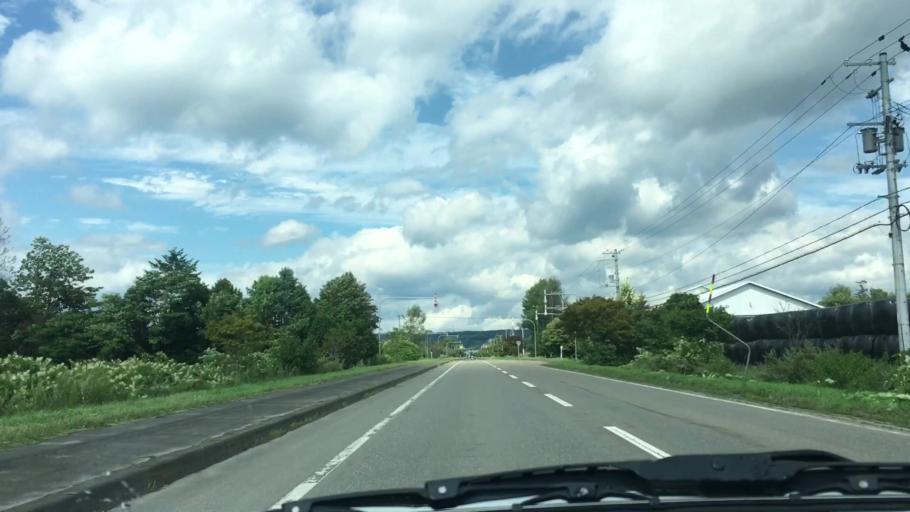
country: JP
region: Hokkaido
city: Otofuke
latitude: 43.2895
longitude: 143.3079
